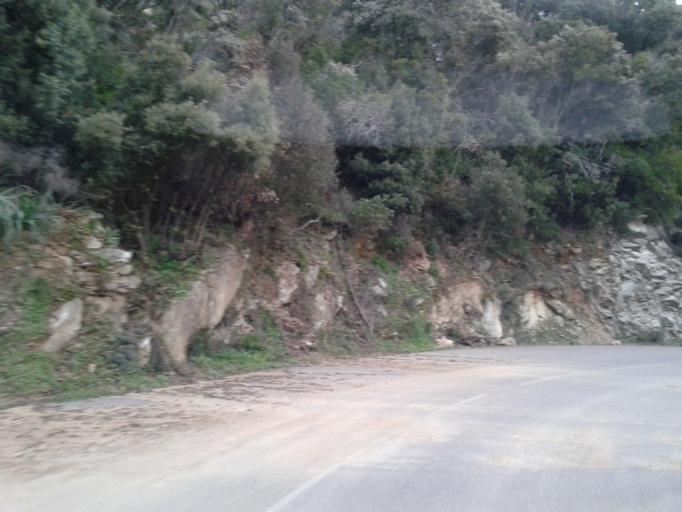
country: FR
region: Corsica
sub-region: Departement de la Haute-Corse
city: Brando
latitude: 42.8697
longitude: 9.3479
